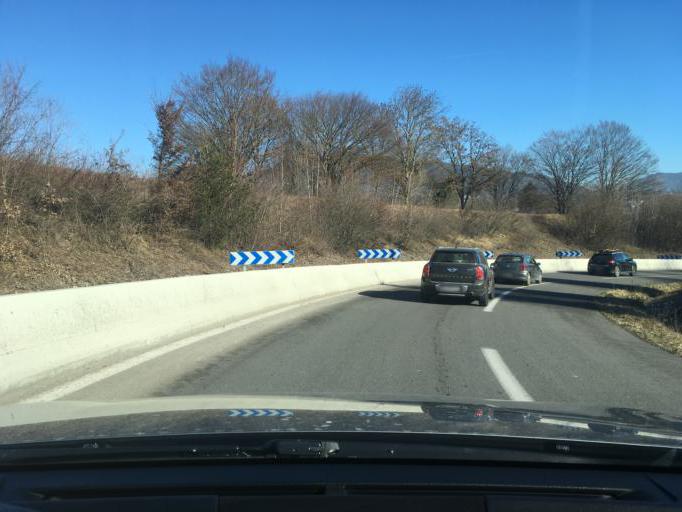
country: FR
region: Rhone-Alpes
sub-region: Departement de la Haute-Savoie
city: Bonne-sur-Menoge
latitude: 46.1411
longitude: 6.3149
